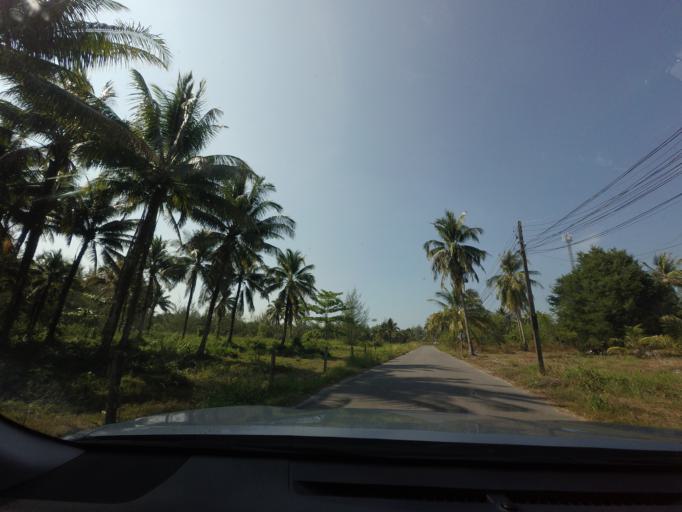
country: TH
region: Phangnga
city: Ban Khao Lak
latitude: 8.7282
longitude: 98.2410
